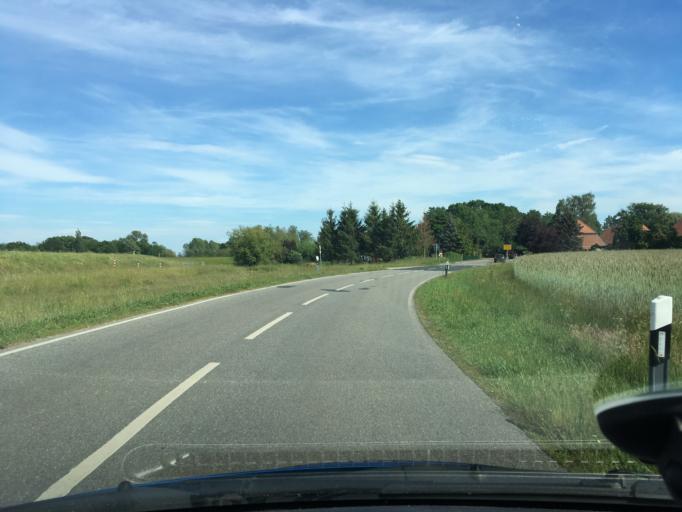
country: DE
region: Lower Saxony
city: Neu Darchau
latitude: 53.3259
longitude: 10.9058
